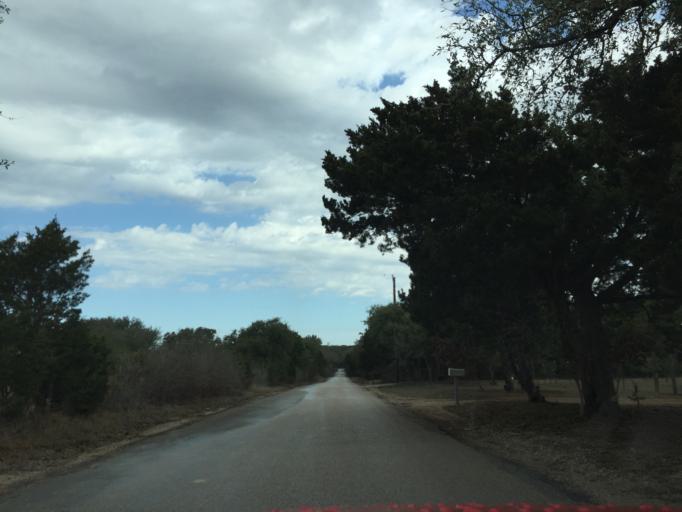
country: US
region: Texas
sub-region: Burnet County
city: Bertram
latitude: 30.6370
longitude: -98.0070
